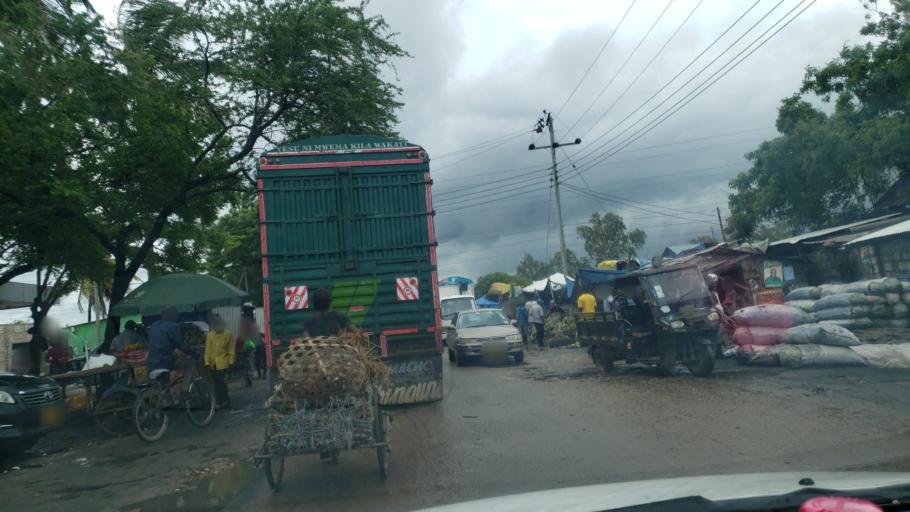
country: TZ
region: Dar es Salaam
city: Magomeni
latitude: -6.8011
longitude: 39.2251
